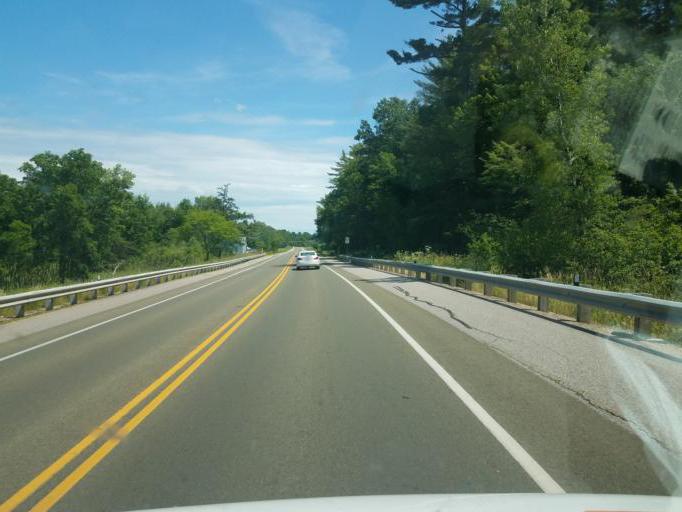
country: US
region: Wisconsin
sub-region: Sauk County
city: Reedsburg
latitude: 43.5771
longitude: -90.1114
